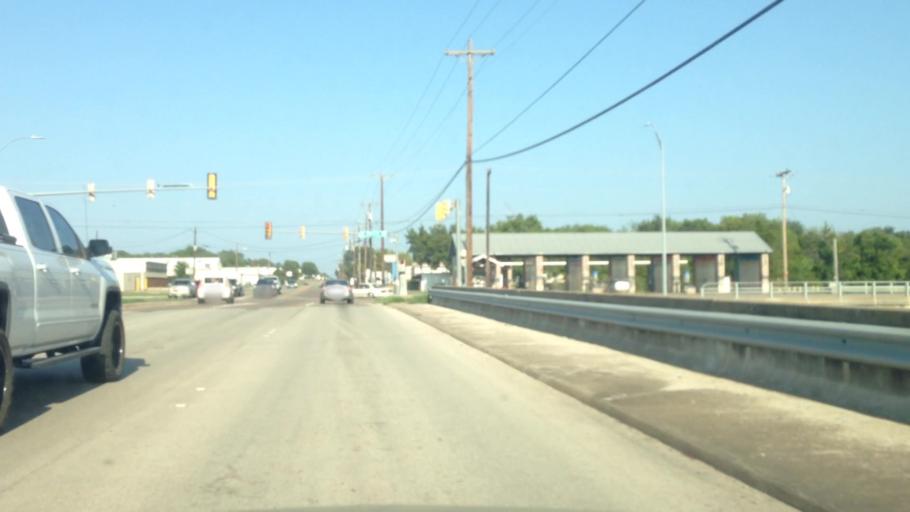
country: US
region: Texas
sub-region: Tarrant County
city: Haltom City
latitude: 32.8097
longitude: -97.2914
